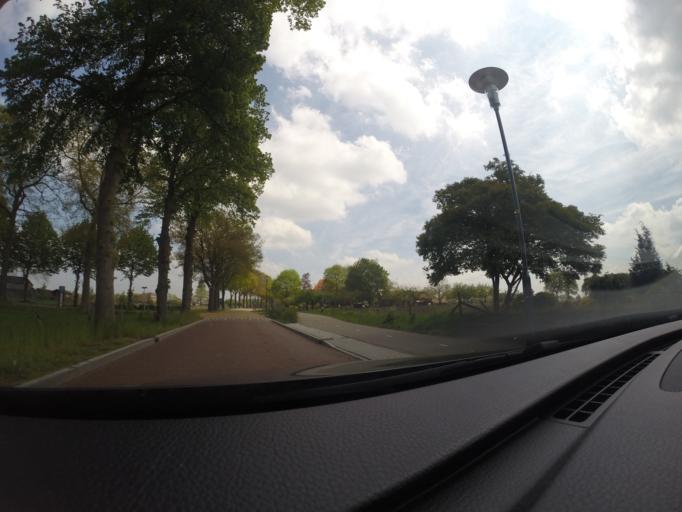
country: NL
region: Gelderland
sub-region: Berkelland
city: Neede
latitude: 52.1122
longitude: 6.5863
